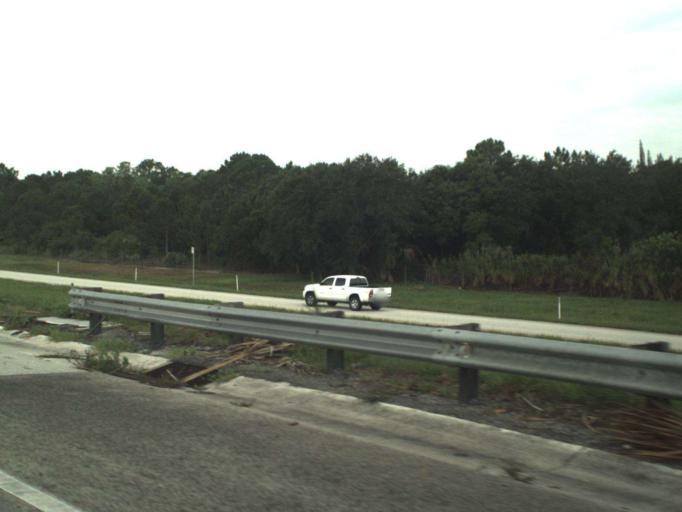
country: US
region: Florida
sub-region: Martin County
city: Palm City
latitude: 27.1060
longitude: -80.2595
